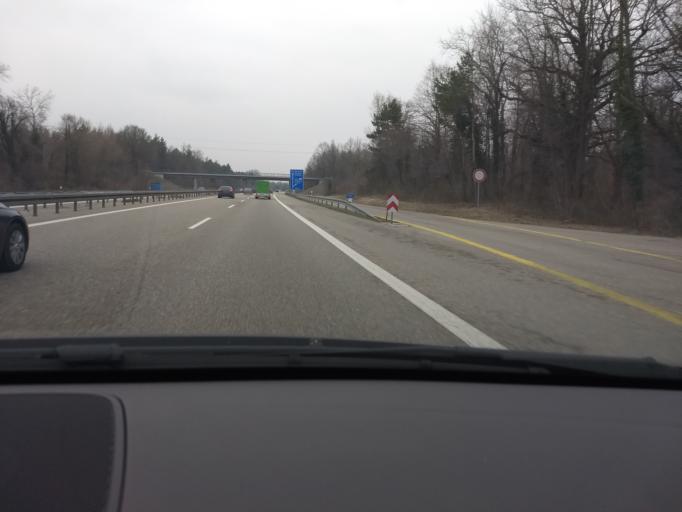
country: FR
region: Alsace
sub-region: Departement du Haut-Rhin
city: Ottmarsheim
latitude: 47.7688
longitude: 7.5376
